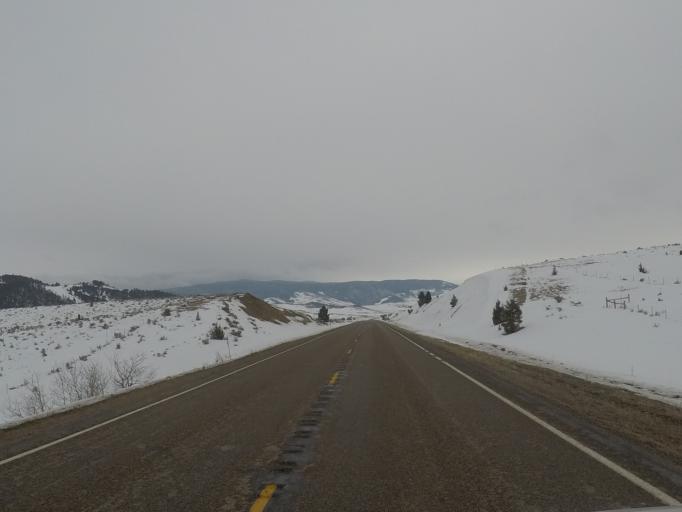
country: US
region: Montana
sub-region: Meagher County
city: White Sulphur Springs
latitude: 46.6223
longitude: -110.8468
